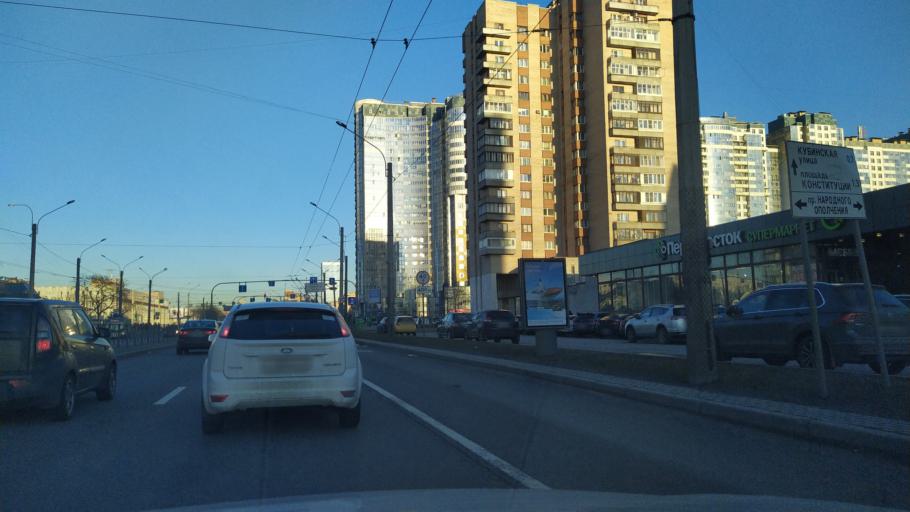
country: RU
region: St.-Petersburg
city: Avtovo
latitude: 59.8518
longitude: 30.2771
